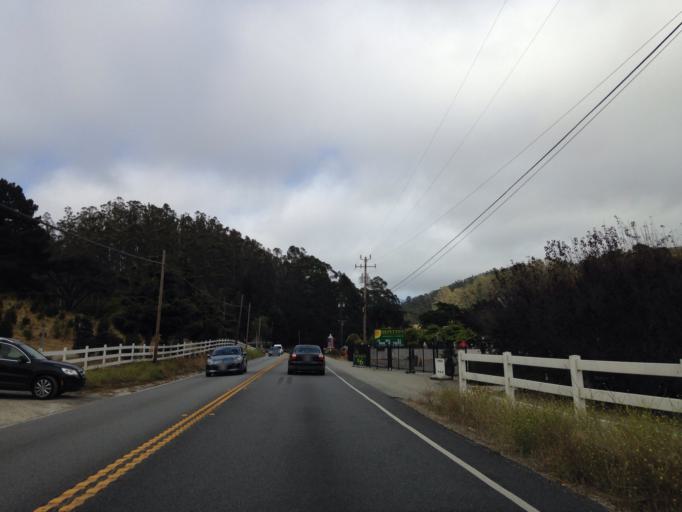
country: US
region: California
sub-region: San Mateo County
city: Half Moon Bay
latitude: 37.4794
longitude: -122.4092
